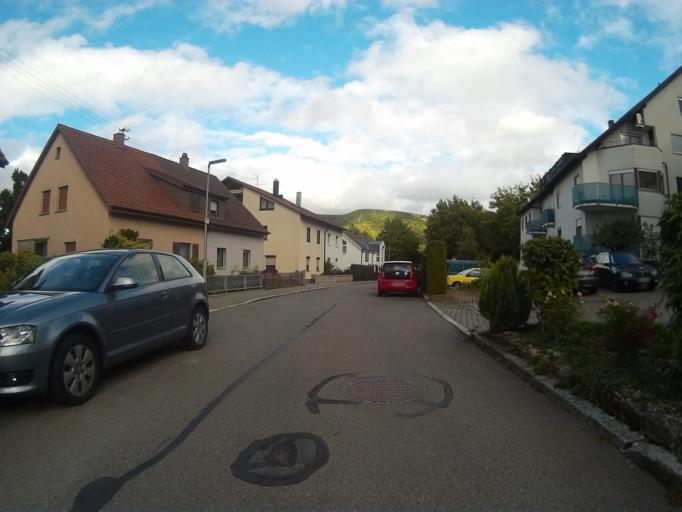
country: DE
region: Baden-Wuerttemberg
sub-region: Tuebingen Region
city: Pfullingen
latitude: 48.4562
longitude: 9.2239
